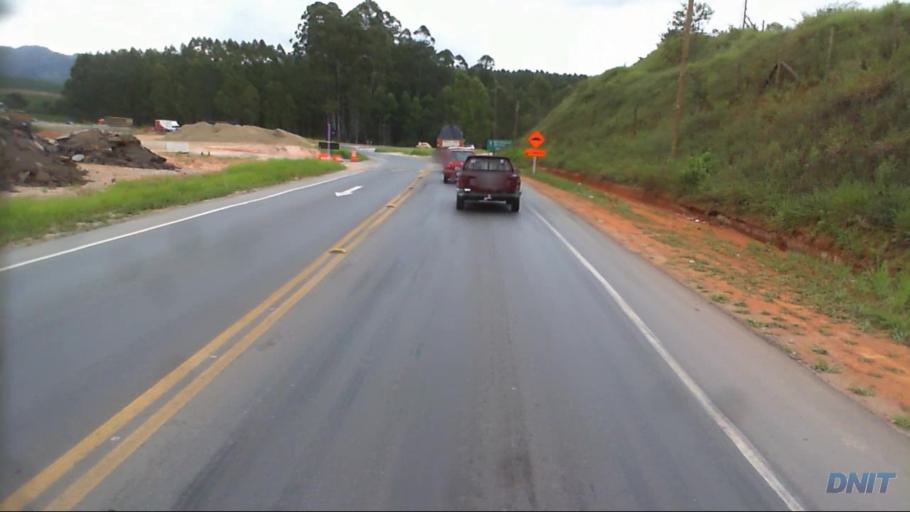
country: BR
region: Minas Gerais
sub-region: Barao De Cocais
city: Barao de Cocais
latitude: -19.7534
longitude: -43.4742
